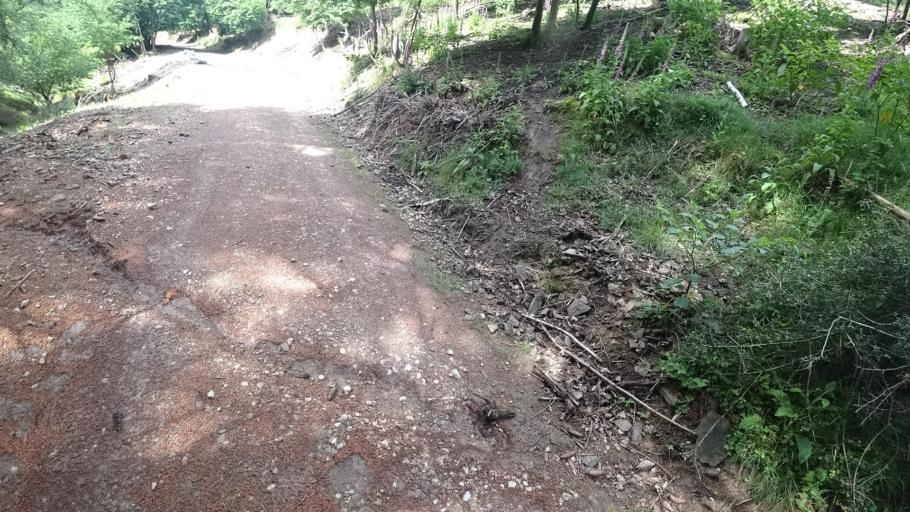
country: DE
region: Rheinland-Pfalz
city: Altenahr
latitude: 50.5342
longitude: 6.9878
